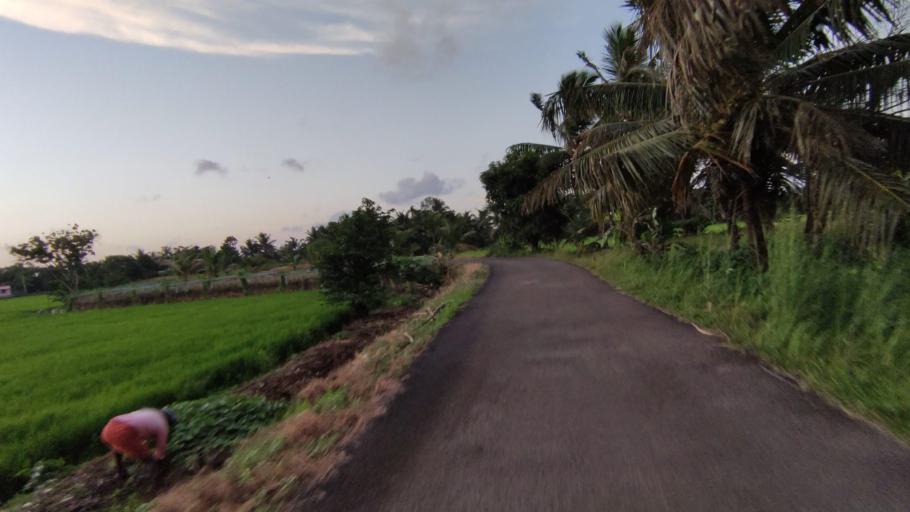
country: IN
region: Kerala
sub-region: Kottayam
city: Kottayam
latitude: 9.5869
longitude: 76.4538
